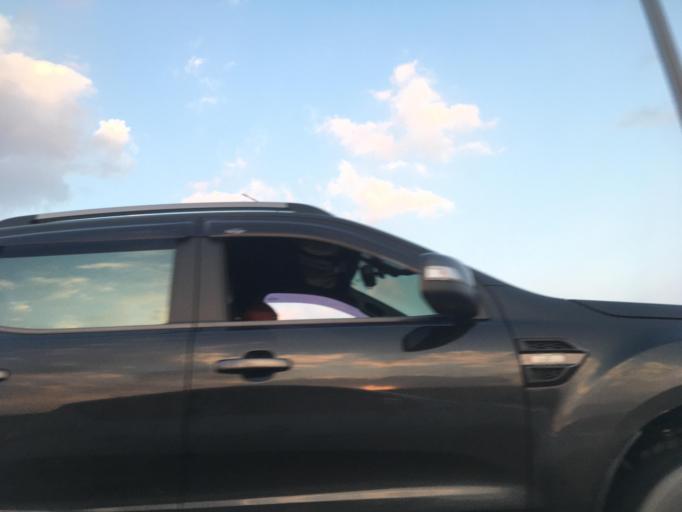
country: TW
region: Taiwan
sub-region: Yilan
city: Yilan
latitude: 24.8085
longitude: 121.7817
